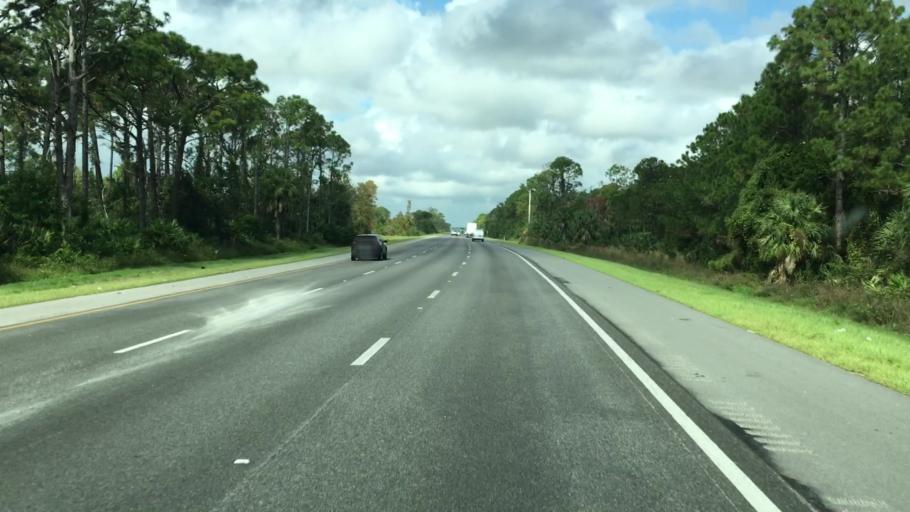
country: US
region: Florida
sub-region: Volusia County
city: Glencoe
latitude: 29.0670
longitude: -81.0092
